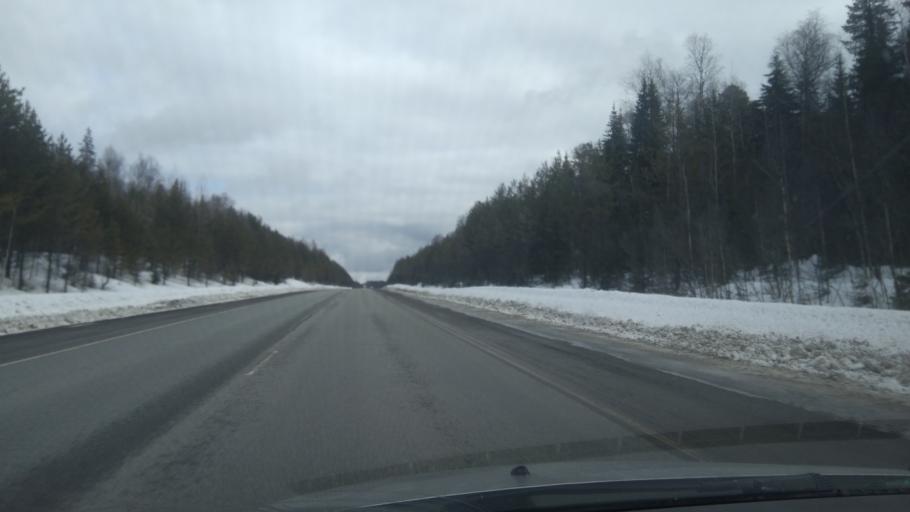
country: RU
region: Sverdlovsk
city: Nizhniye Sergi
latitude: 56.8249
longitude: 59.2726
